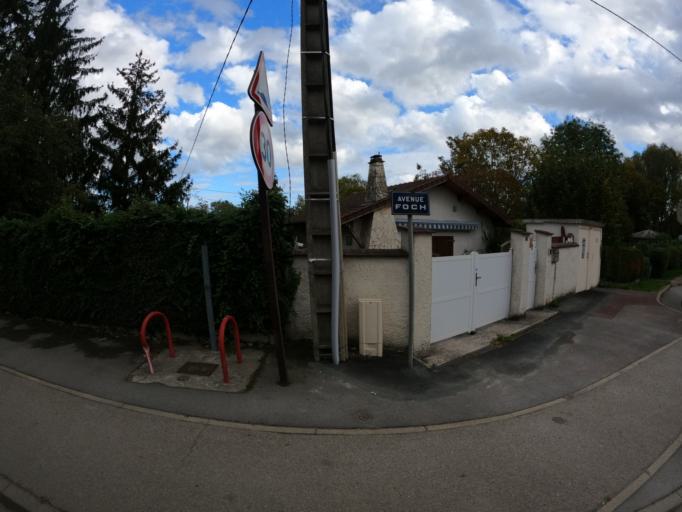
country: FR
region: Ile-de-France
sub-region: Departement de Seine-et-Marne
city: Esbly
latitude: 48.9088
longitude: 2.8149
